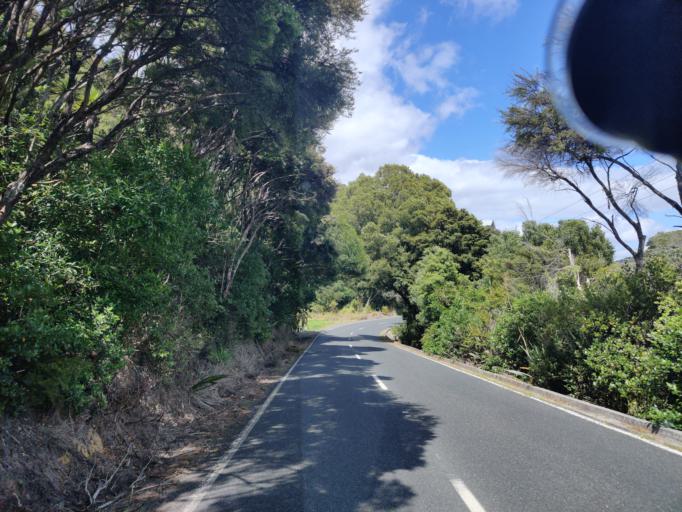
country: NZ
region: Northland
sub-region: Far North District
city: Paihia
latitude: -35.2567
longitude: 174.2369
